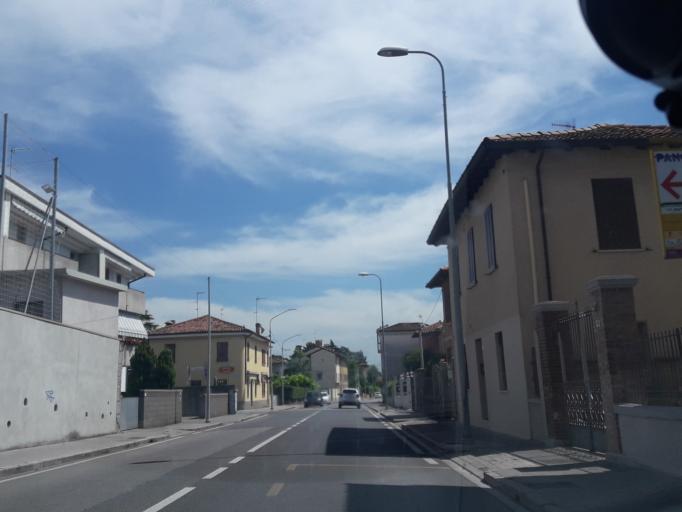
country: IT
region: Friuli Venezia Giulia
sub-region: Provincia di Udine
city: Udine
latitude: 46.0514
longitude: 13.2389
